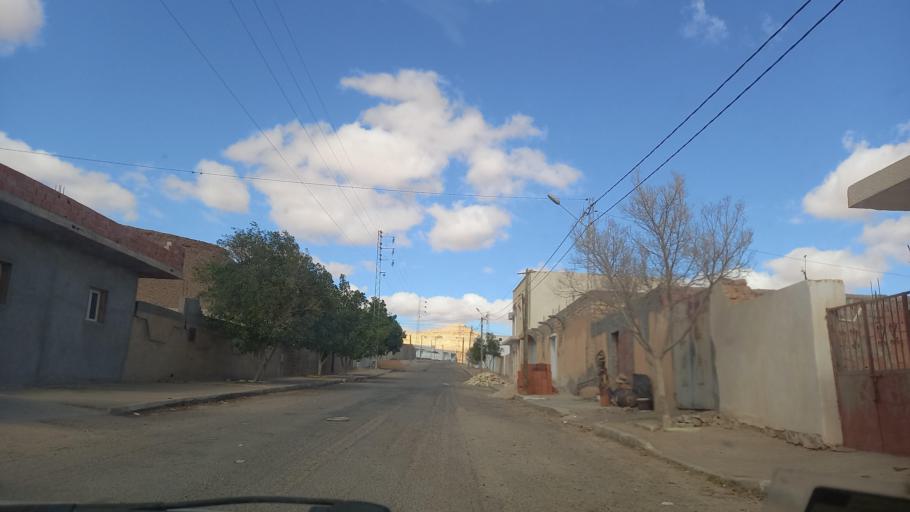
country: TN
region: Tataouine
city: Tataouine
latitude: 32.9817
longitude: 10.2653
